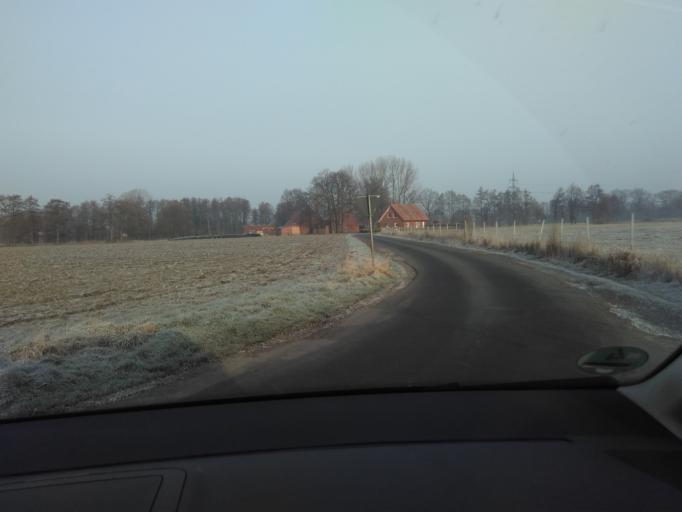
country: DE
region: North Rhine-Westphalia
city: Rietberg
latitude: 51.8455
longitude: 8.4606
